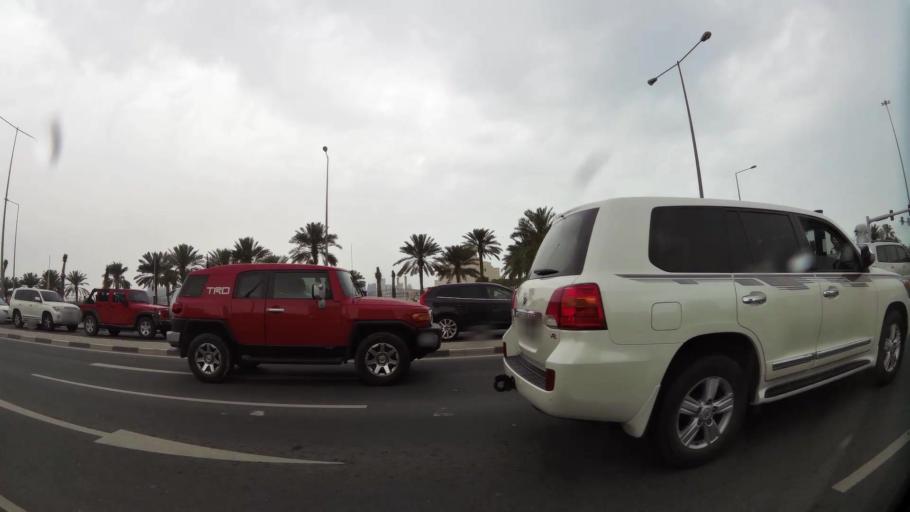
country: QA
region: Baladiyat ad Dawhah
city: Doha
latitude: 25.2909
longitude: 51.5388
